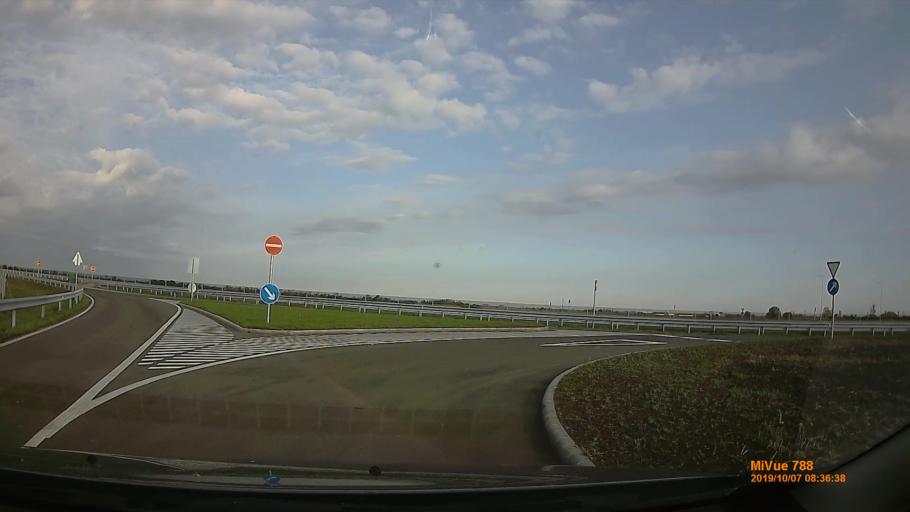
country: HU
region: Bekes
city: Bekesszentandras
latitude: 46.8262
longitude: 20.4718
